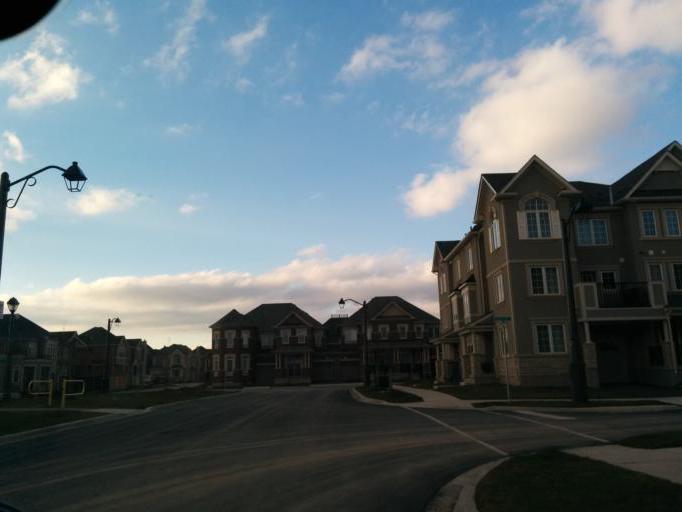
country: CA
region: Ontario
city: Oakville
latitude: 43.4747
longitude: -79.7378
